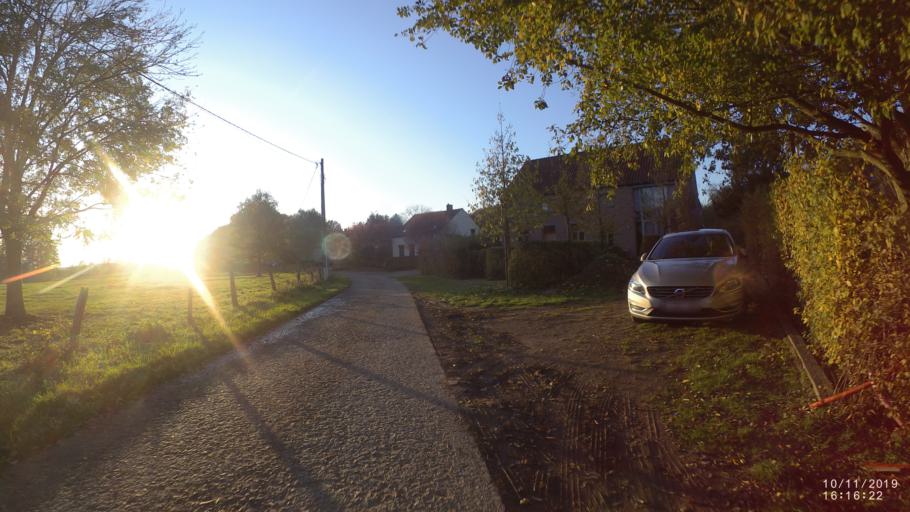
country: BE
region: Flanders
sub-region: Provincie Vlaams-Brabant
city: Lubbeek
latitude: 50.8940
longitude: 4.8525
